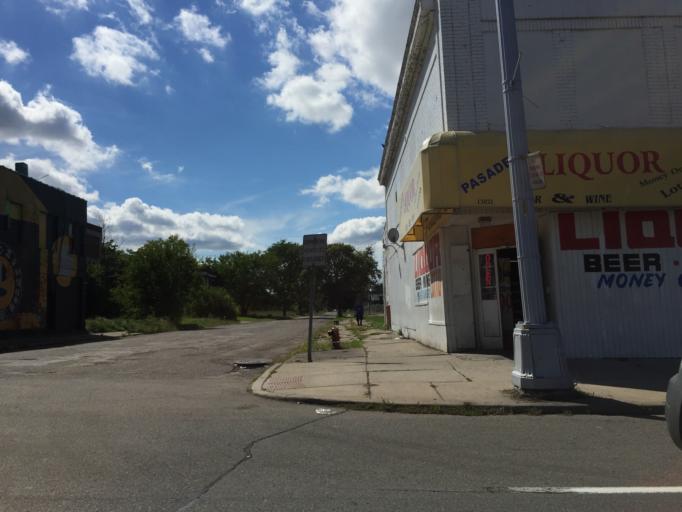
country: US
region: Michigan
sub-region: Wayne County
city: Highland Park
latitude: 42.4051
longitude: -83.0968
